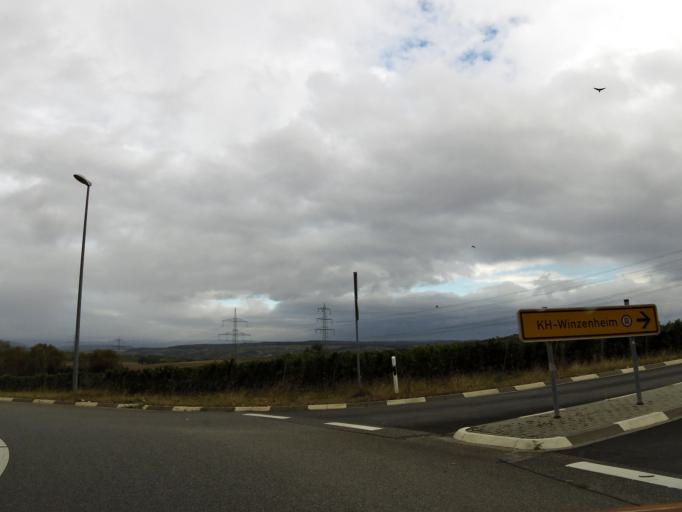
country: DE
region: Rheinland-Pfalz
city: Hargesheim
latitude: 49.8703
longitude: 7.8509
